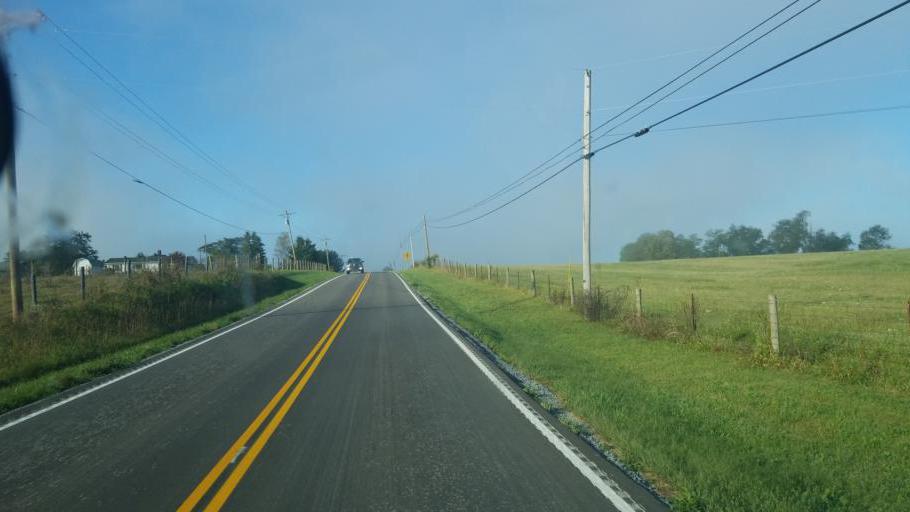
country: US
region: Kentucky
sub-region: Fleming County
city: Flemingsburg
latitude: 38.4726
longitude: -83.6681
